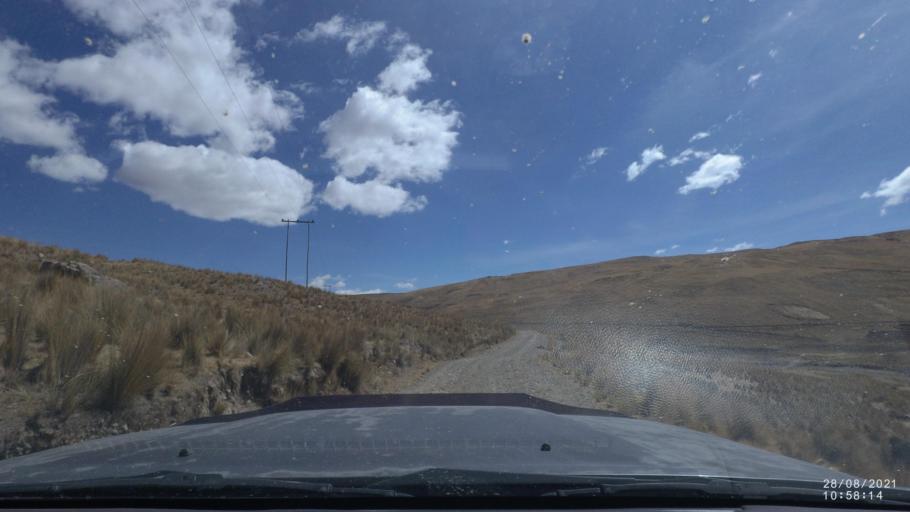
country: BO
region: Cochabamba
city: Cochabamba
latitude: -17.1868
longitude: -66.2536
